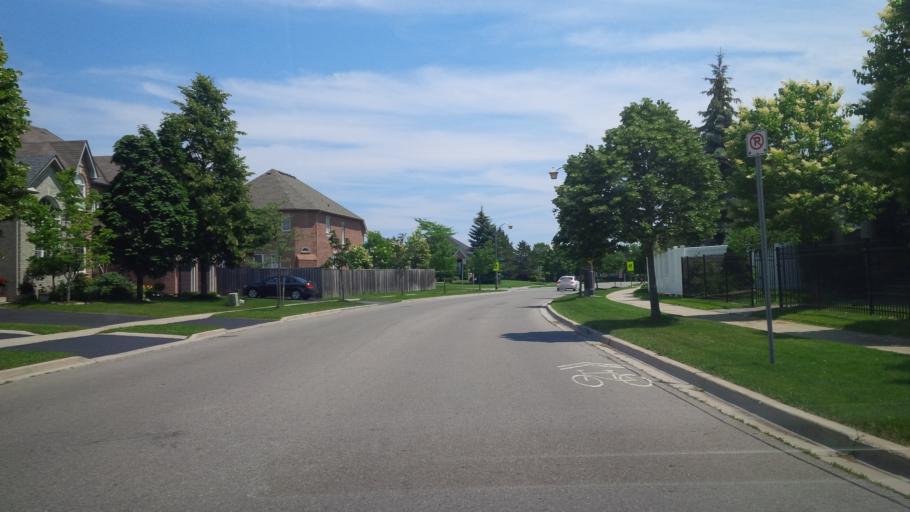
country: CA
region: Ontario
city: Burlington
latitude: 43.3986
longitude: -79.8055
